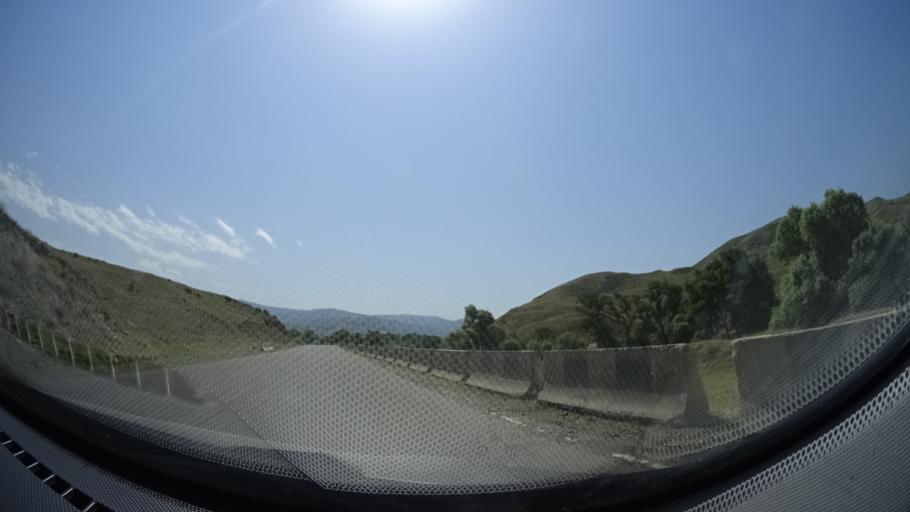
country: GE
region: Samtskhe-Javakheti
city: Aspindza
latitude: 41.5958
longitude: 43.2103
